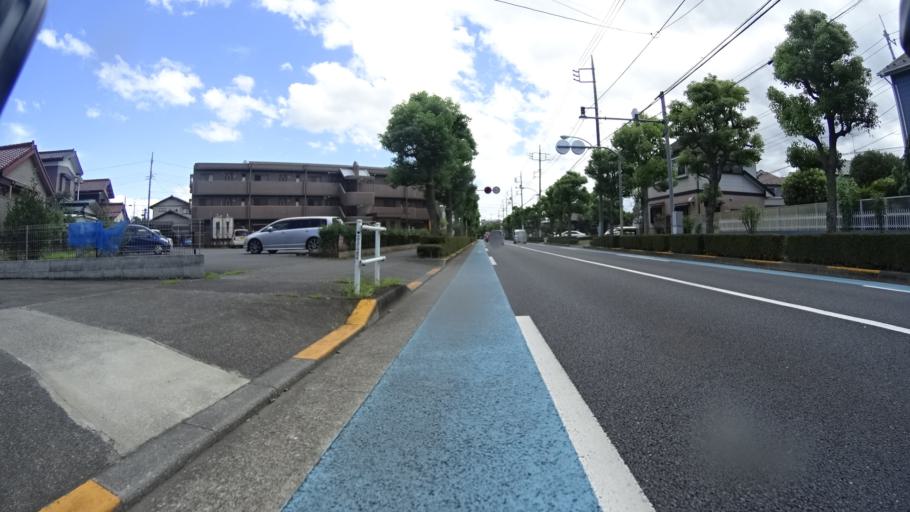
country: JP
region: Tokyo
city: Fussa
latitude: 35.7635
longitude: 139.3094
